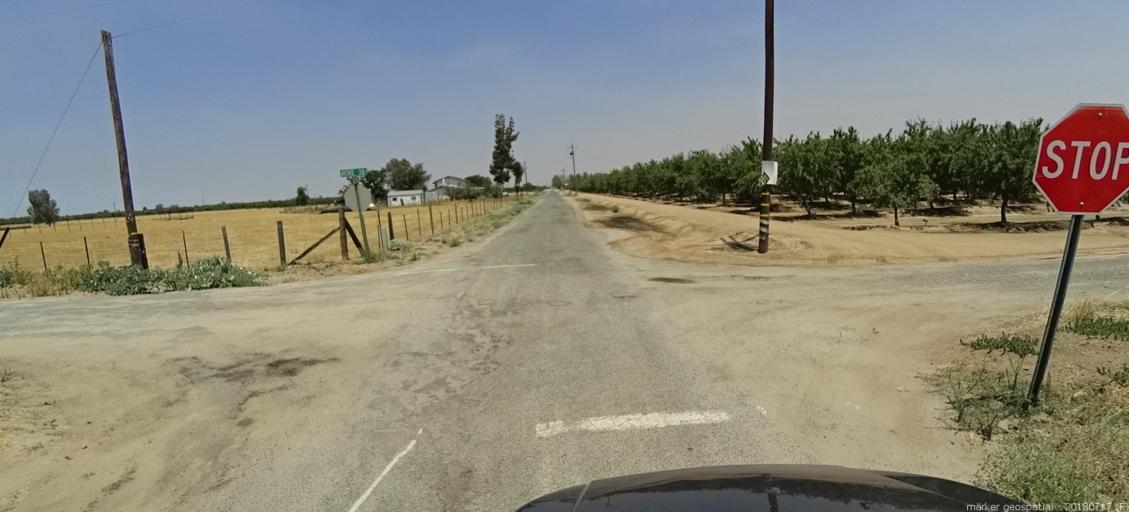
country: US
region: California
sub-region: Madera County
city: Fairmead
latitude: 37.1339
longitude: -120.1292
